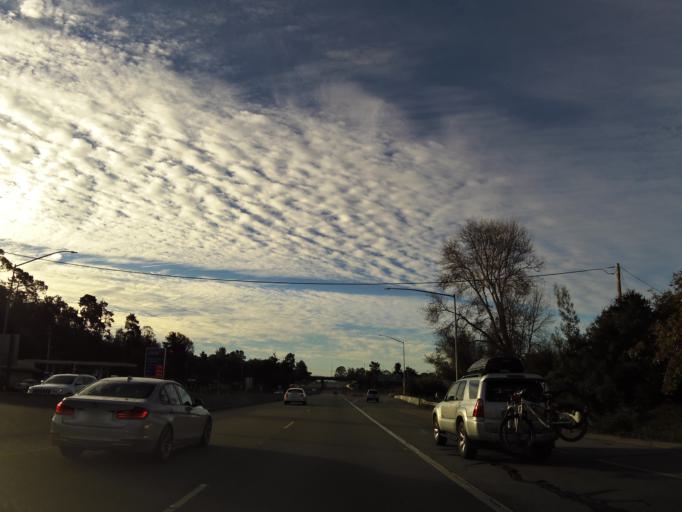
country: US
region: California
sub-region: Monterey County
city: Prunedale
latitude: 36.7928
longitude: -121.6670
